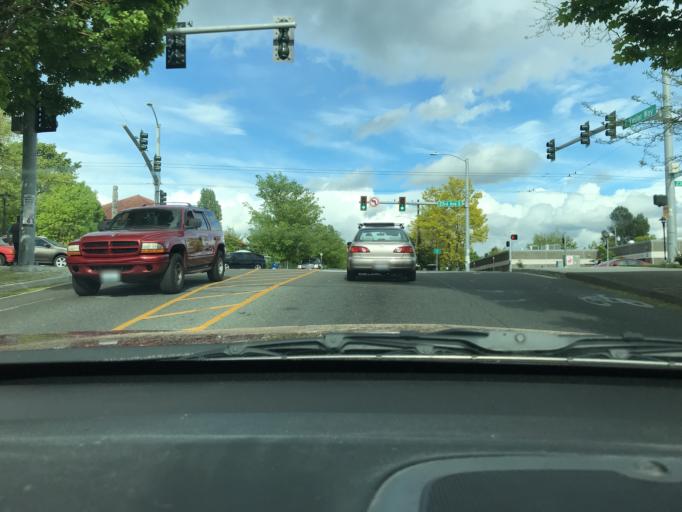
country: US
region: Washington
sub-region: King County
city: Seattle
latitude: 47.6017
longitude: -122.3029
